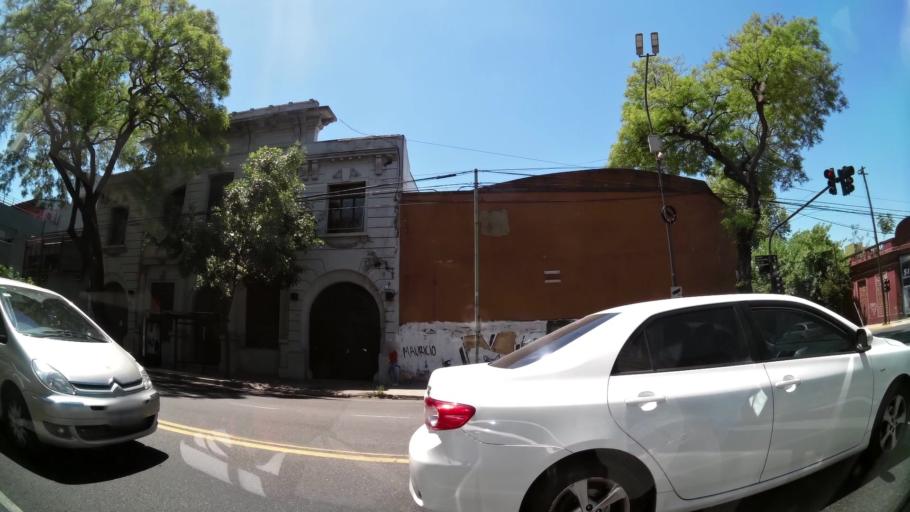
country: AR
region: Buenos Aires
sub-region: Partido de Avellaneda
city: Avellaneda
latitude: -34.6428
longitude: -58.3897
